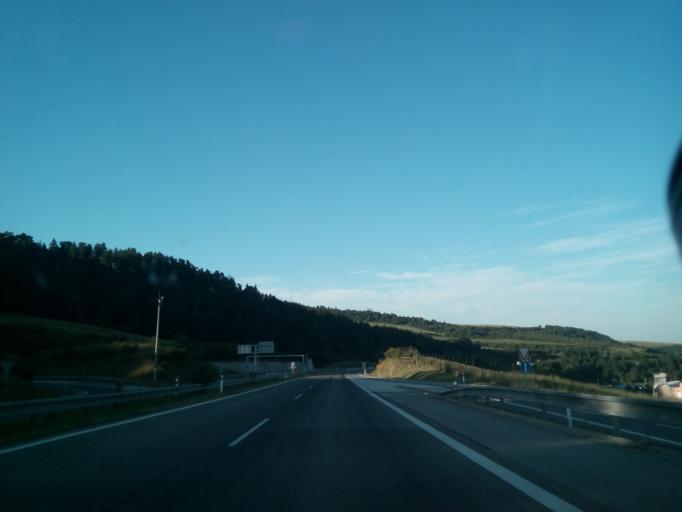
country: SK
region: Kosicky
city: Krompachy
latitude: 49.0112
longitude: 20.9414
